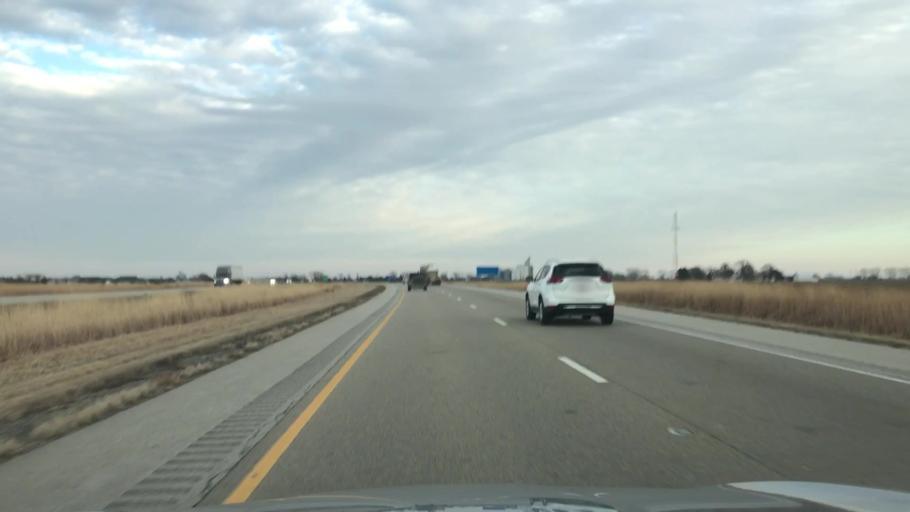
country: US
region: Illinois
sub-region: Logan County
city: Lincoln
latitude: 40.1816
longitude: -89.3474
